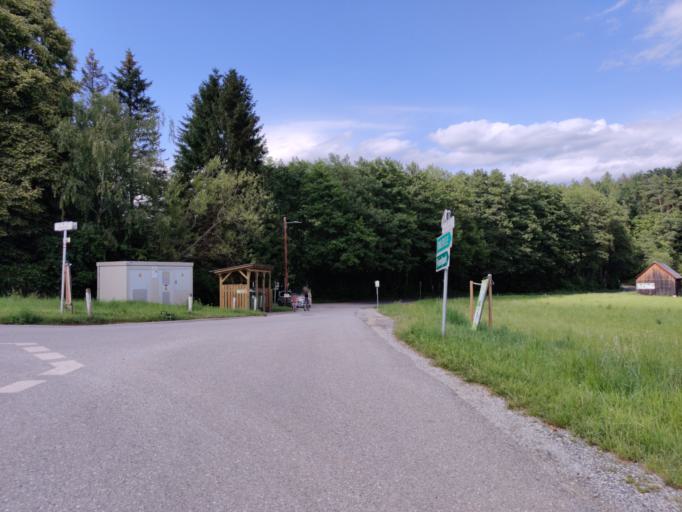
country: AT
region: Styria
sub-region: Politischer Bezirk Graz-Umgebung
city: Thal
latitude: 47.0724
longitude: 15.3355
